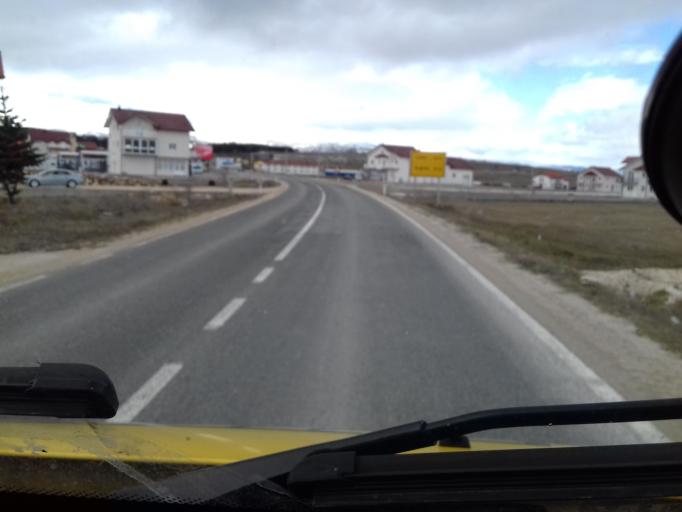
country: BA
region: Federation of Bosnia and Herzegovina
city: Tomislavgrad
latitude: 43.7168
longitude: 17.2381
